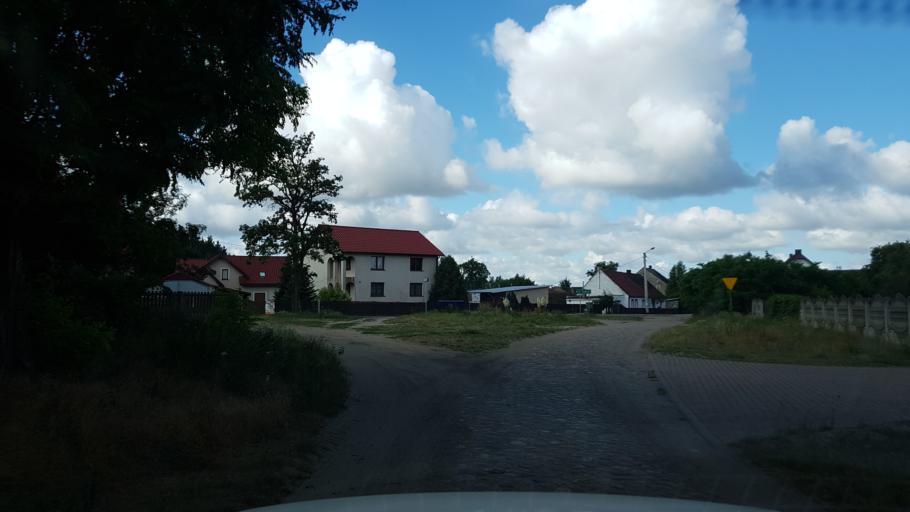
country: PL
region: West Pomeranian Voivodeship
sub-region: Powiat mysliborski
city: Debno
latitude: 52.7126
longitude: 14.6570
